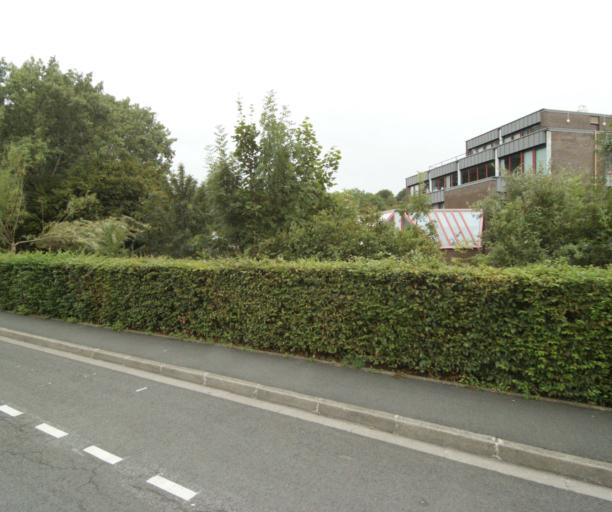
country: FR
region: Nord-Pas-de-Calais
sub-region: Departement du Nord
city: Lezennes
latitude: 50.6207
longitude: 3.1269
